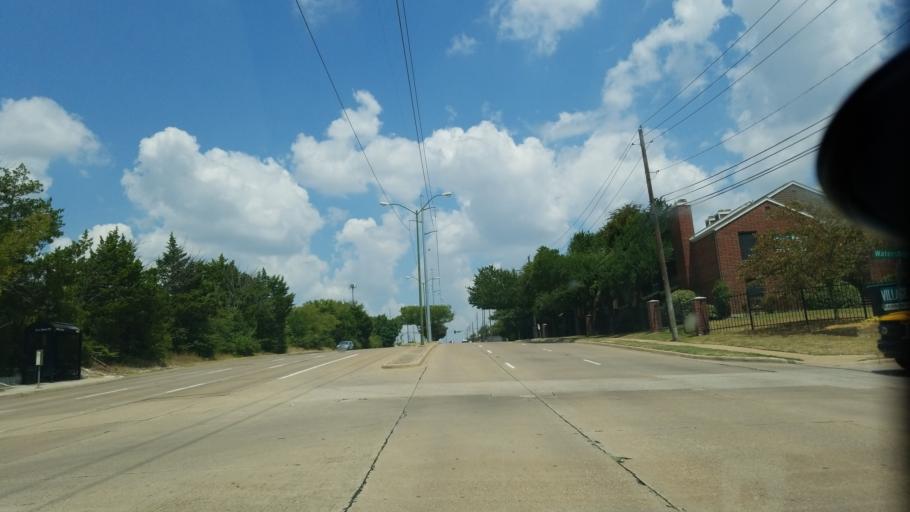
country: US
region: Texas
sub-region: Dallas County
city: Duncanville
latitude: 32.6742
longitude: -96.8827
